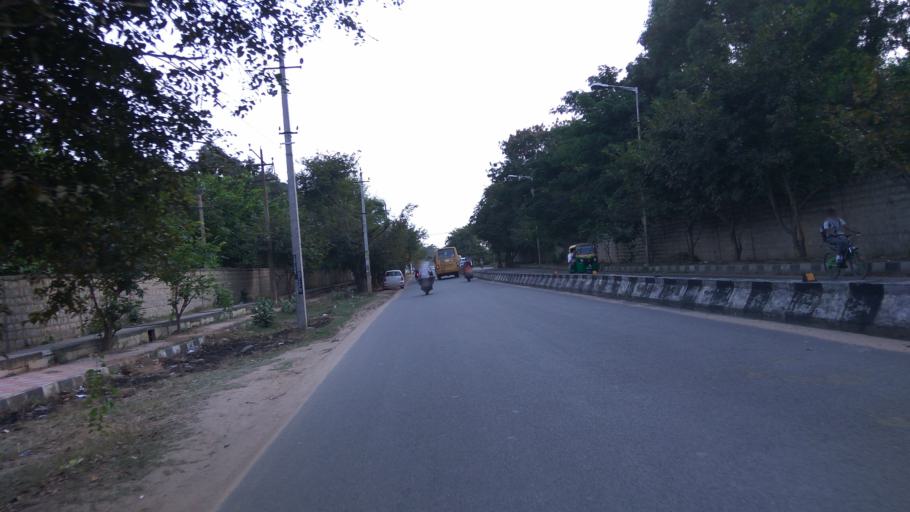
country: IN
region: Karnataka
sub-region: Bangalore Urban
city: Bangalore
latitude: 12.9625
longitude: 77.6904
